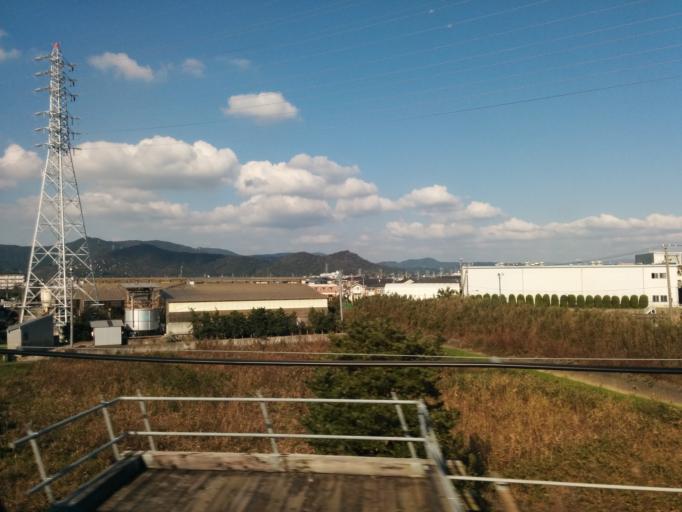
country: JP
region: Shizuoka
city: Kosai-shi
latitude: 34.7139
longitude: 137.4886
